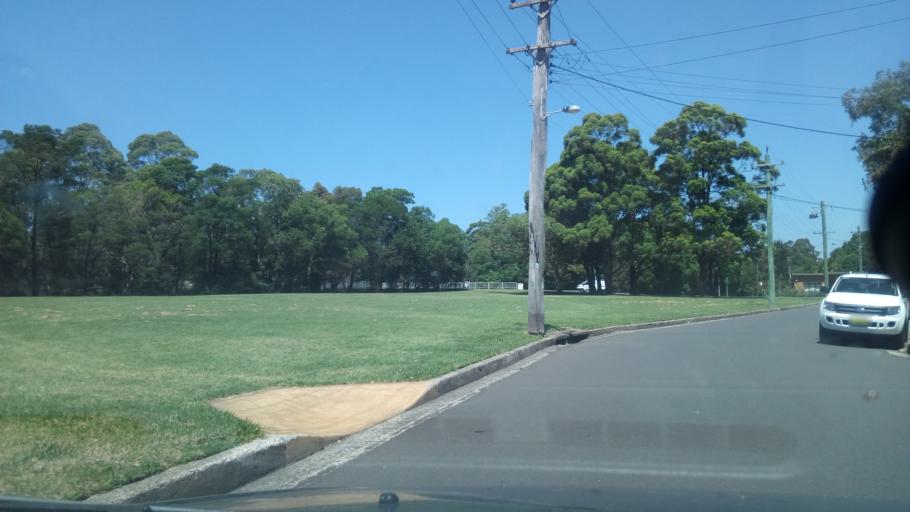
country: AU
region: New South Wales
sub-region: Wollongong
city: West Wollongong
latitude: -34.4259
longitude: 150.8599
